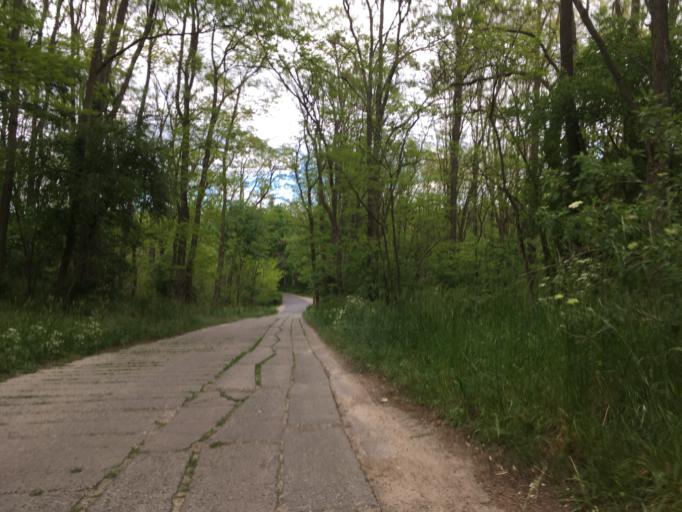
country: DE
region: Brandenburg
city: Hohenfinow
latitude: 52.7652
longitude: 13.9064
